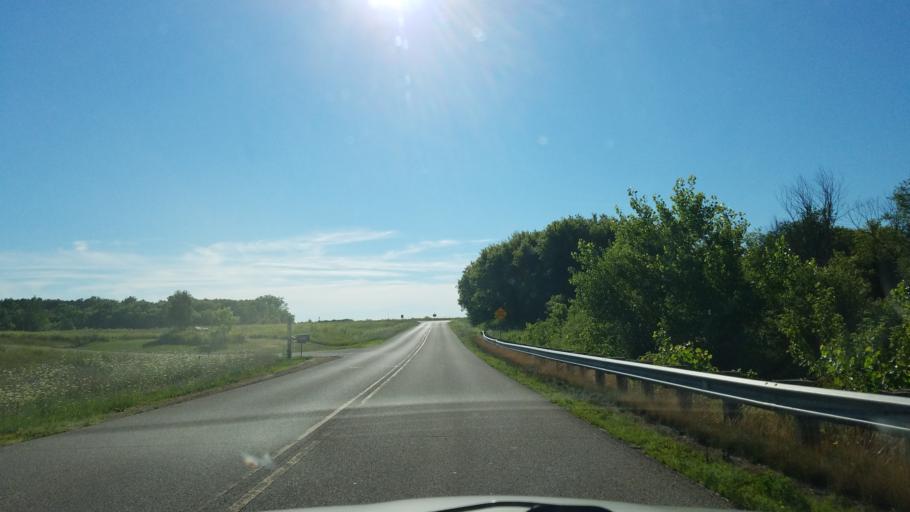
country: US
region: Wisconsin
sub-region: Saint Croix County
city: Somerset
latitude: 45.1109
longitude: -92.7238
